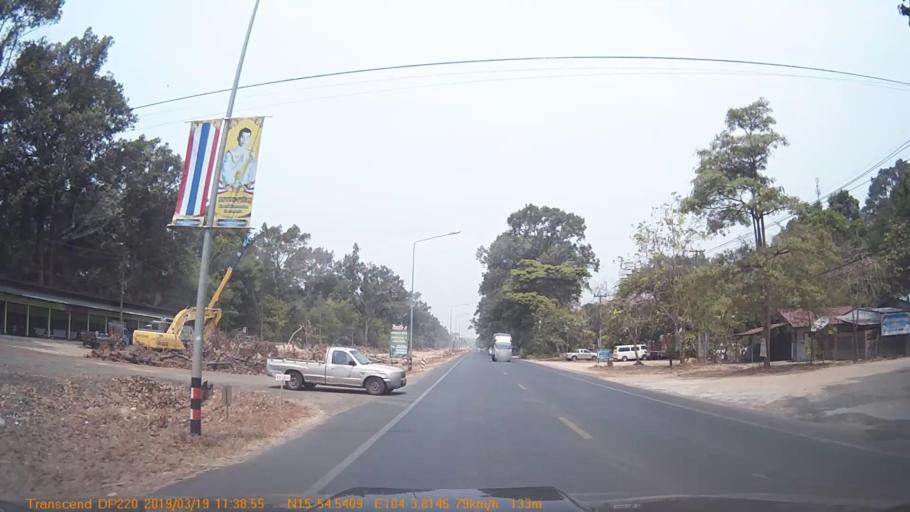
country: TH
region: Yasothon
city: Yasothon
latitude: 15.9092
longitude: 104.0635
